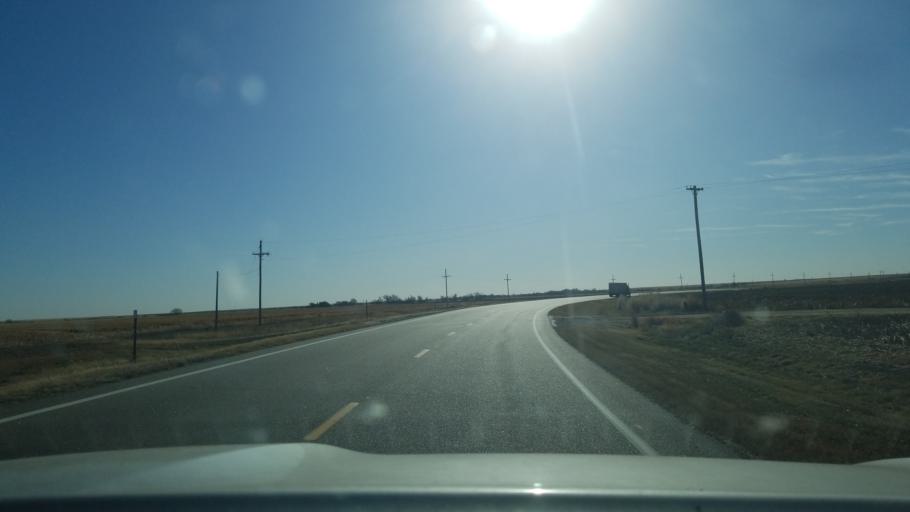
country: US
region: Kansas
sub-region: Ness County
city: Ness City
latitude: 38.4289
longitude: -99.9002
